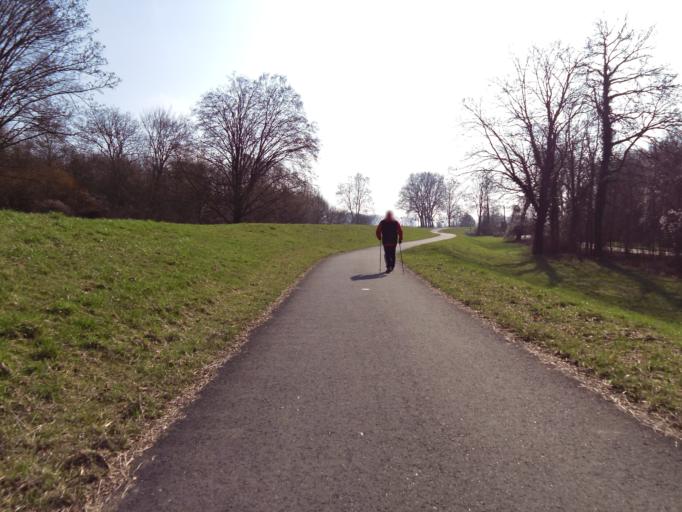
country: DE
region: Rheinland-Pfalz
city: Bobenheim-Roxheim
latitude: 49.6080
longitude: 8.3980
